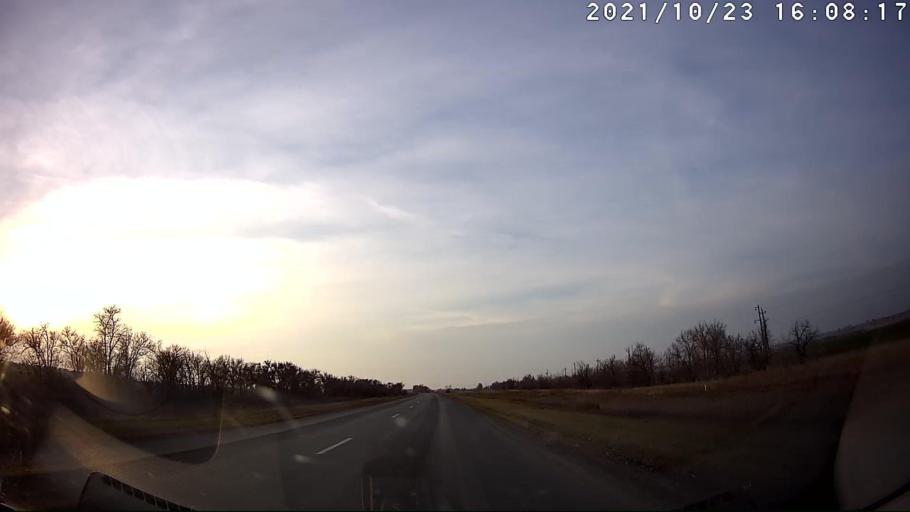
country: RU
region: Volgograd
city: Kotel'nikovo
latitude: 47.9400
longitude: 43.7209
